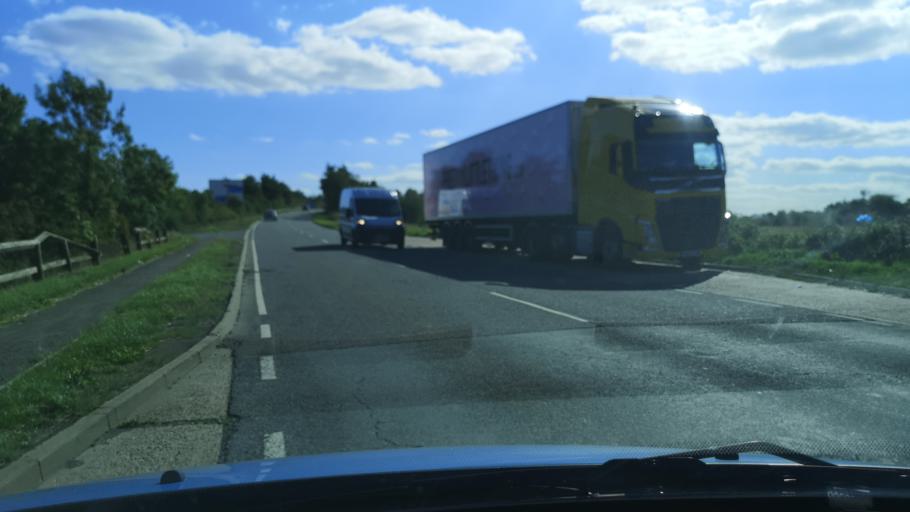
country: GB
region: England
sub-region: North Lincolnshire
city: Belton
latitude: 53.5727
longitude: -0.8175
